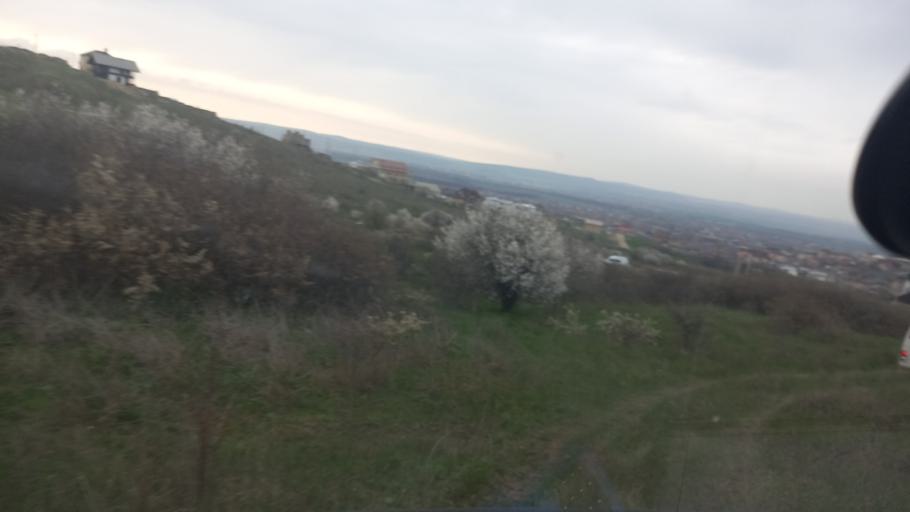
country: RU
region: Krasnodarskiy
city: Anapa
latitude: 44.8525
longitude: 37.3436
